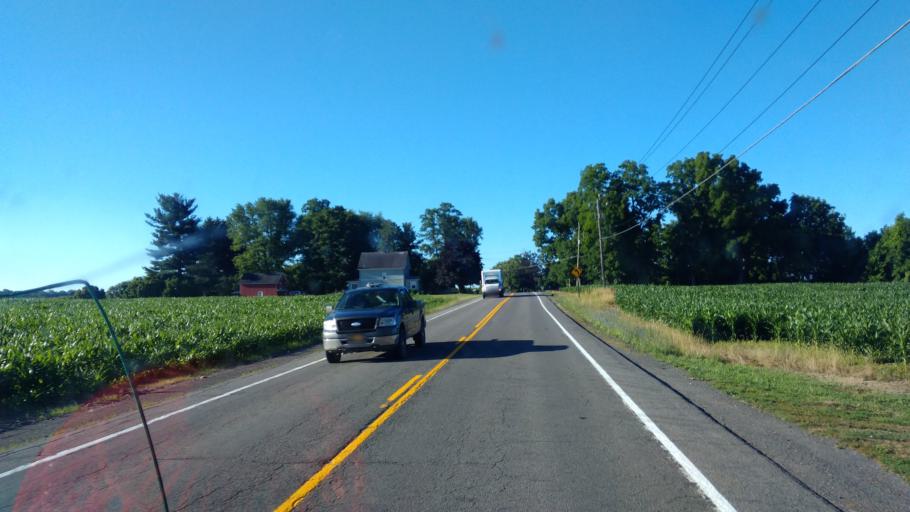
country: US
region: New York
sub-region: Wayne County
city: Lyons
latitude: 43.0304
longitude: -76.9916
